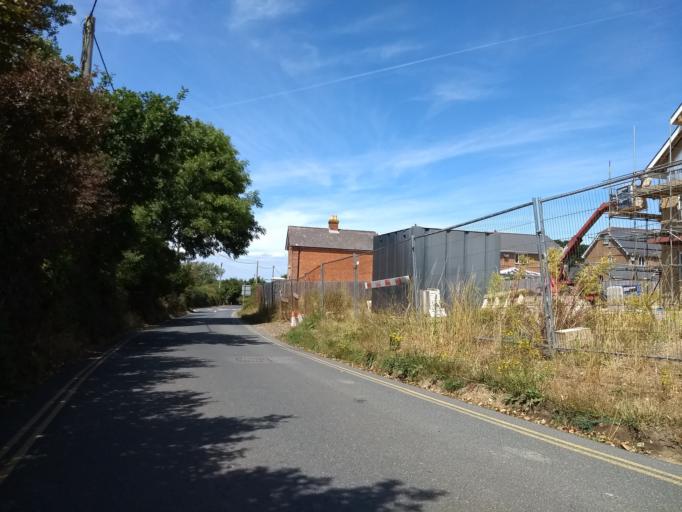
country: GB
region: England
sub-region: Isle of Wight
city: Gurnard
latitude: 50.7524
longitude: -1.3232
